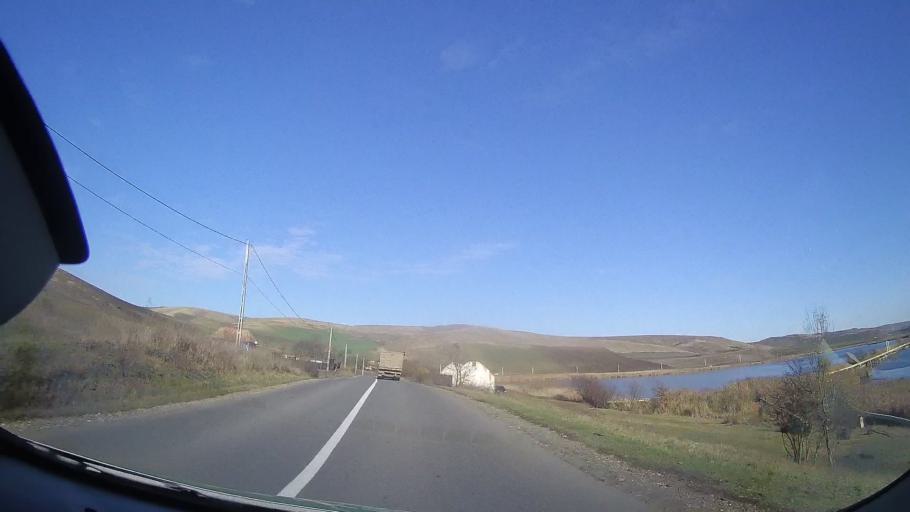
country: RO
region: Mures
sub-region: Comuna Zau De Campie
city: Zau de Campie
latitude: 46.6451
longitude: 24.1465
